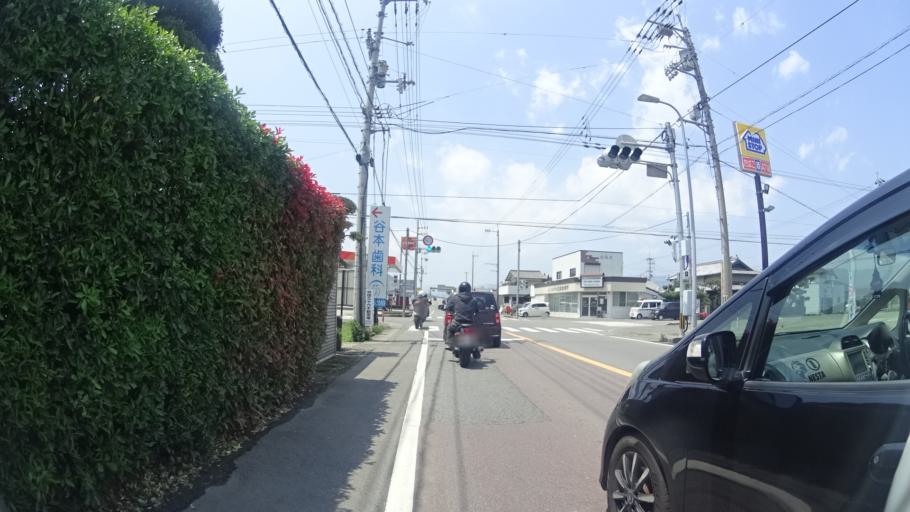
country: JP
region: Tokushima
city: Wakimachi
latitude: 34.0569
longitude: 134.2316
